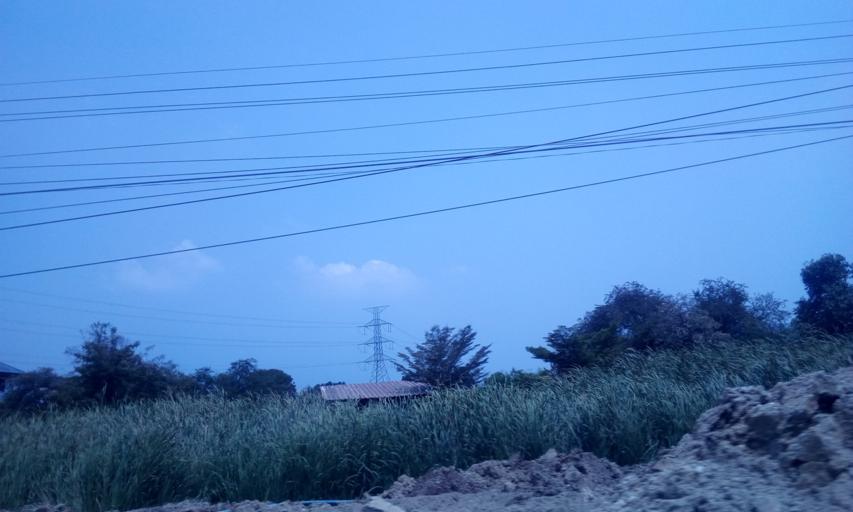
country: TH
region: Chachoengsao
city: Ban Pho
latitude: 13.5756
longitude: 101.1257
